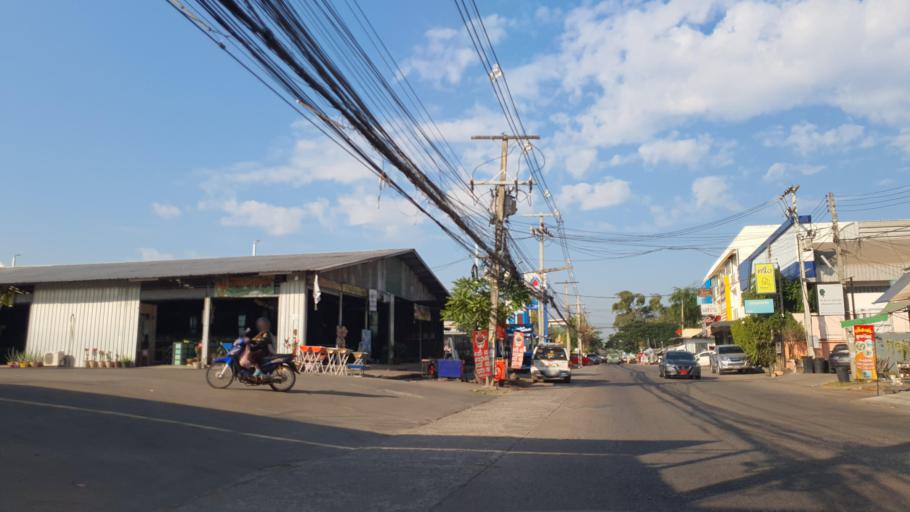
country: TH
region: Khon Kaen
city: Khon Kaen
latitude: 16.4213
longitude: 102.8108
